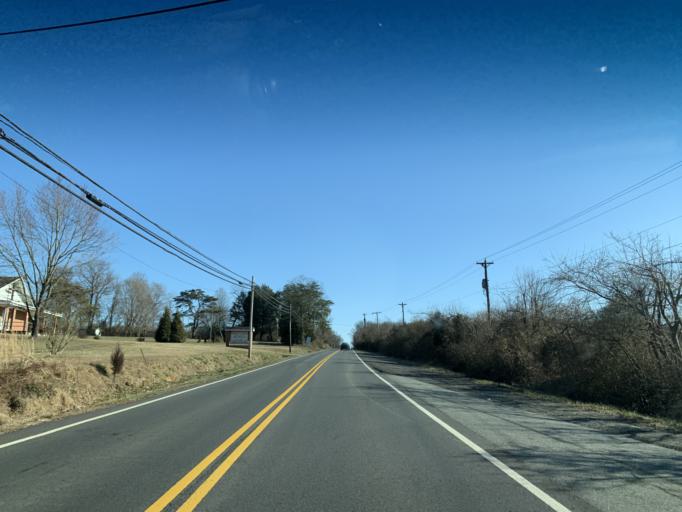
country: US
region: Maryland
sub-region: Cecil County
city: Elkton
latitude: 39.6300
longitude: -75.8582
